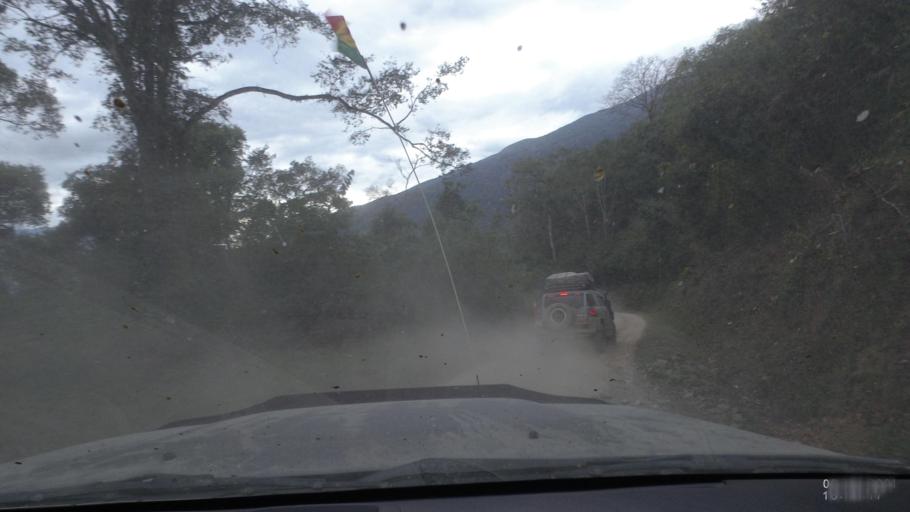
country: BO
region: La Paz
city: Quime
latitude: -16.5158
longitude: -66.7670
